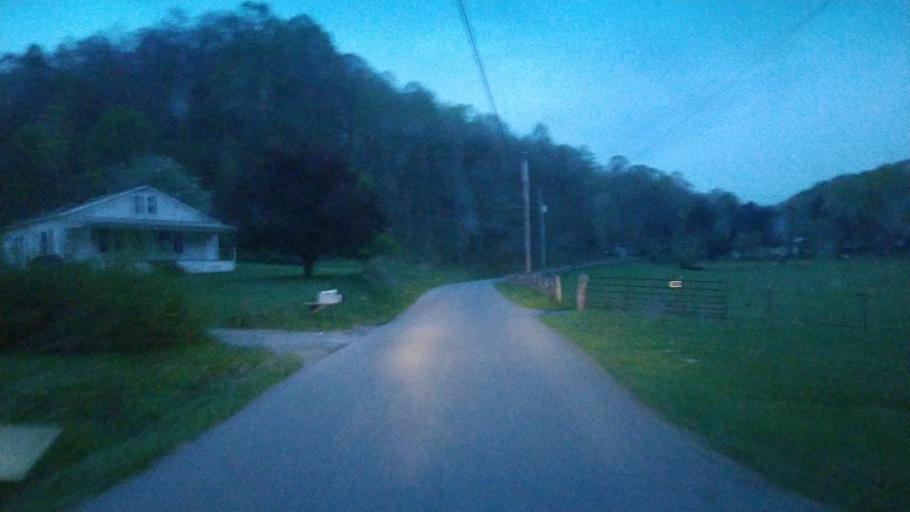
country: US
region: Virginia
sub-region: Smyth County
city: Atkins
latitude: 36.8327
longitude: -81.4560
